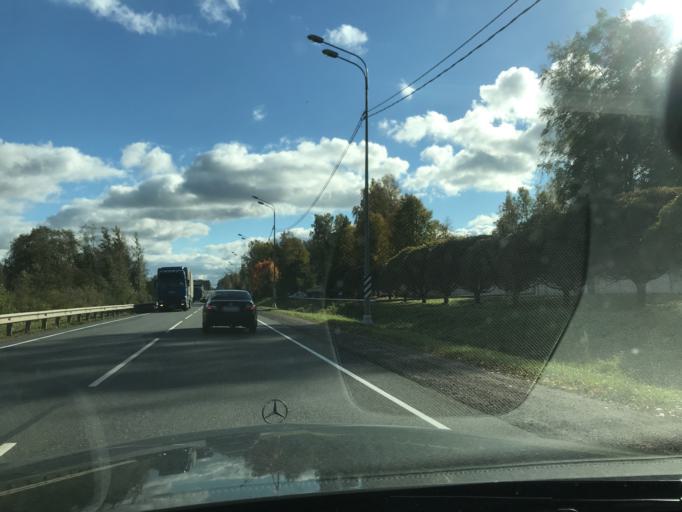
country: RU
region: Pskov
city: Ostrov
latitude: 57.1829
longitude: 28.4777
